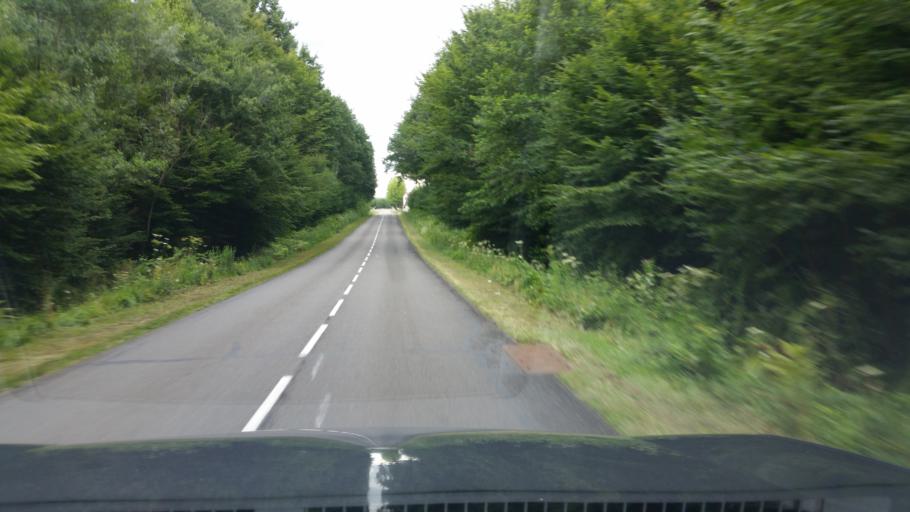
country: FR
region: Franche-Comte
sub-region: Departement du Jura
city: Bletterans
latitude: 46.6759
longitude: 5.3881
